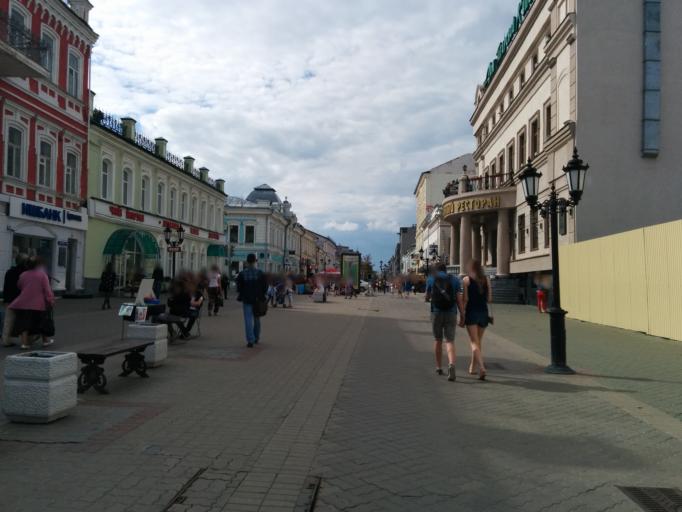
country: RU
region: Tatarstan
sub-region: Gorod Kazan'
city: Kazan
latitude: 55.7895
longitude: 49.1175
